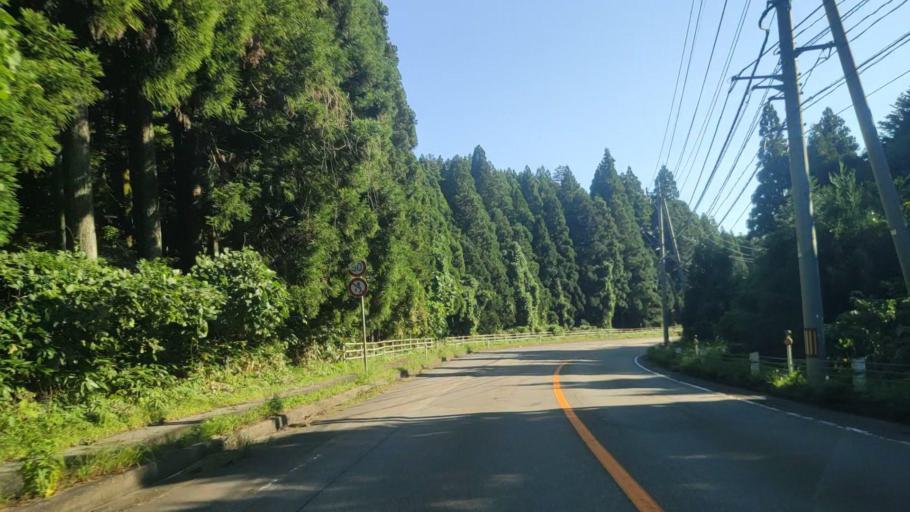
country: JP
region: Ishikawa
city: Nanao
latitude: 37.1217
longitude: 136.8624
